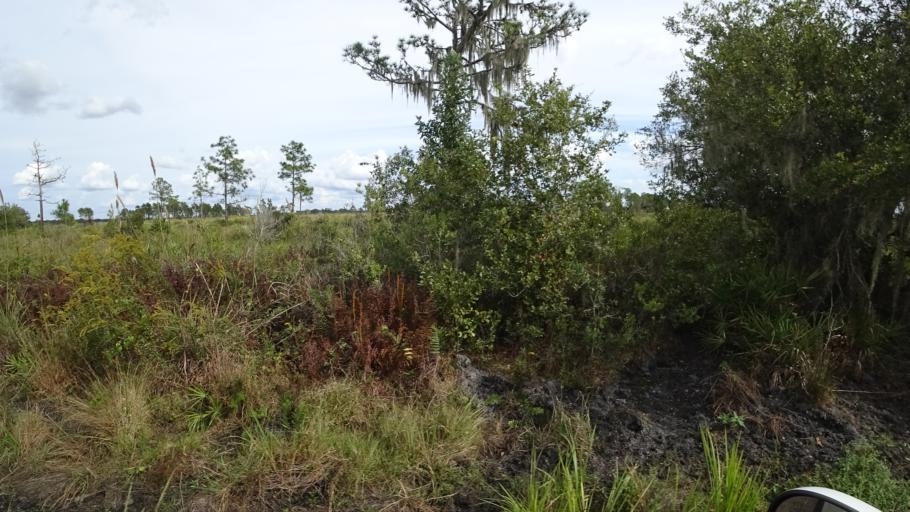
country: US
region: Florida
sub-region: Hillsborough County
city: Wimauma
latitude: 27.5533
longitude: -82.1432
